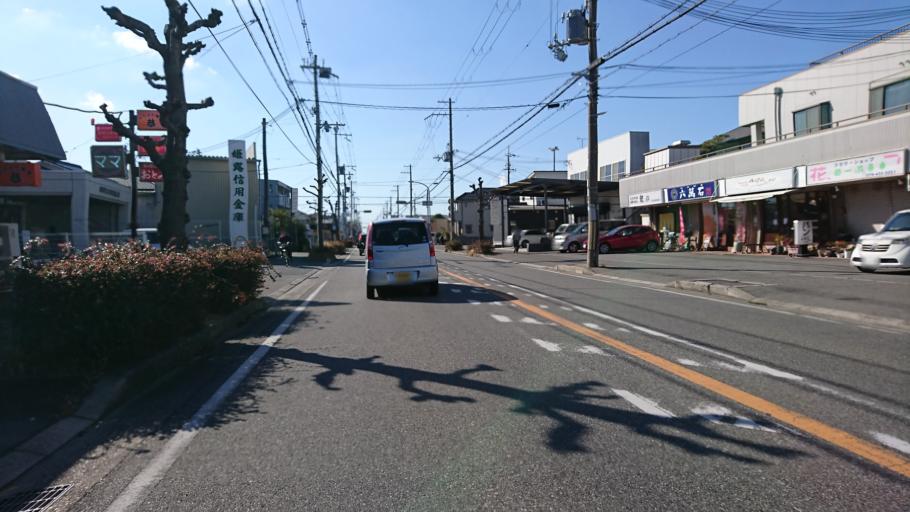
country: JP
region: Hyogo
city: Kakogawacho-honmachi
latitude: 34.7808
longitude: 134.8088
